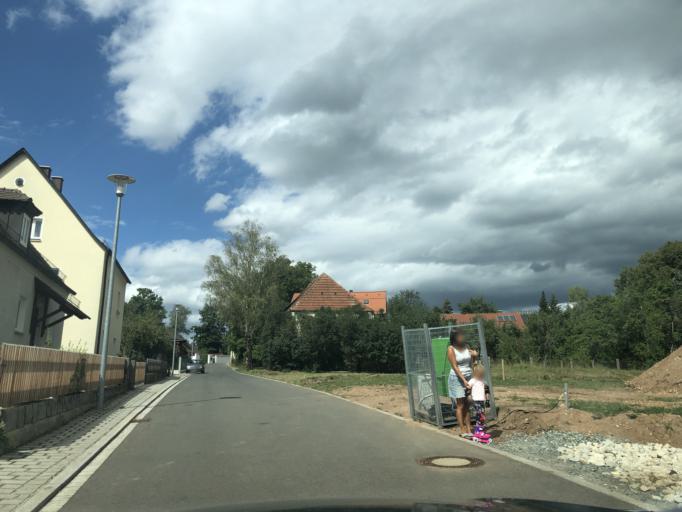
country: DE
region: Bavaria
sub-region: Upper Palatinate
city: Pressath
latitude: 49.7710
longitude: 11.9360
